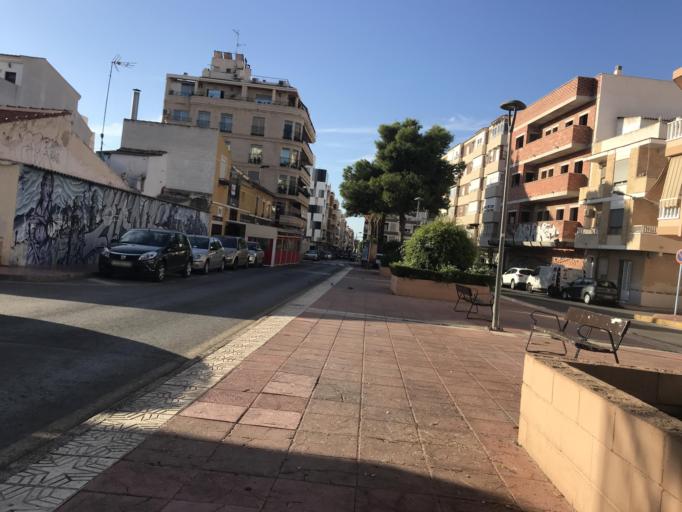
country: ES
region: Valencia
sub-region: Provincia de Alicante
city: Torrevieja
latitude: 37.9796
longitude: -0.6840
